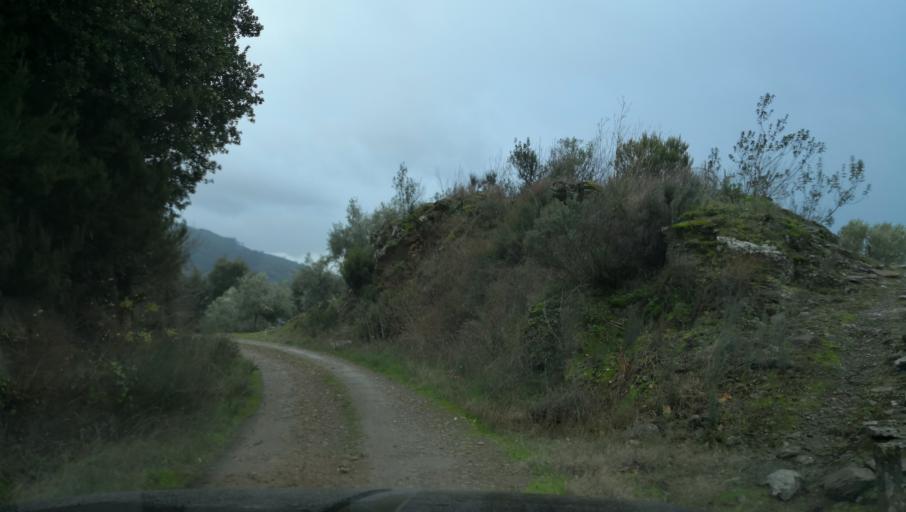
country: PT
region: Vila Real
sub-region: Vila Real
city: Vila Real
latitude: 41.2432
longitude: -7.7500
